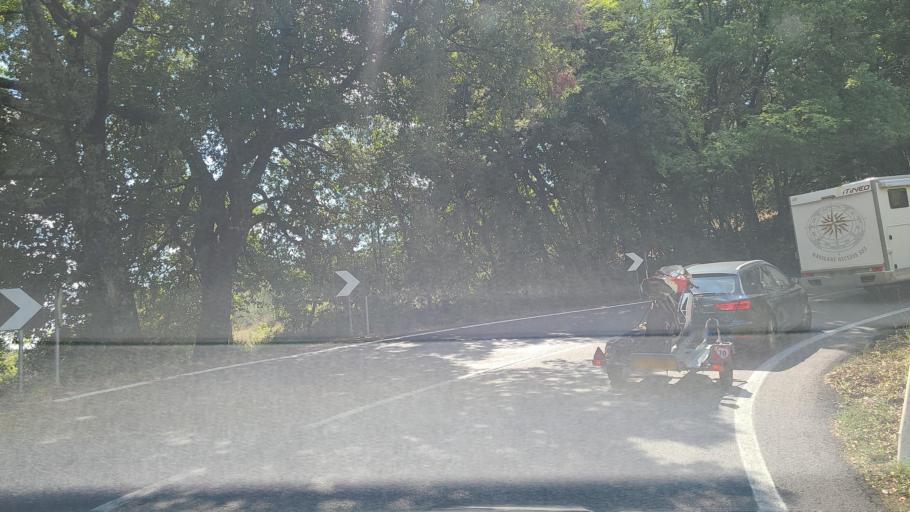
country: IT
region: Tuscany
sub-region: Provincia di Siena
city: Casole d'Elsa
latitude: 43.4014
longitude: 11.0028
